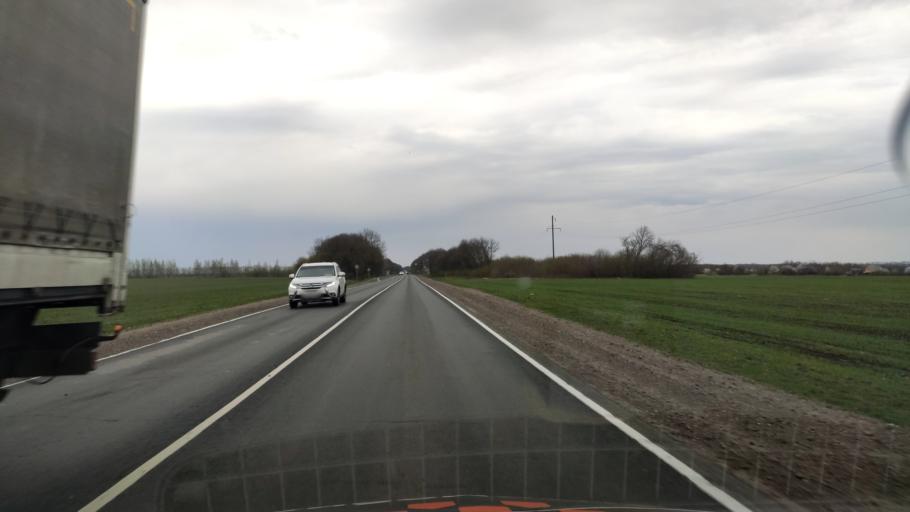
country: RU
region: Voronezj
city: Latnaya
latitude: 51.6492
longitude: 38.7489
